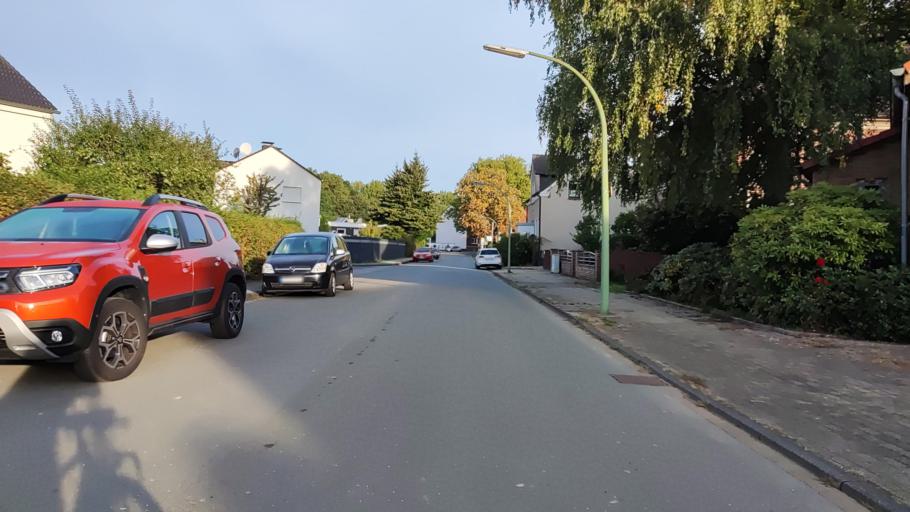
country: DE
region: North Rhine-Westphalia
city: Castrop-Rauxel
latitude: 51.5518
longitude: 7.2837
